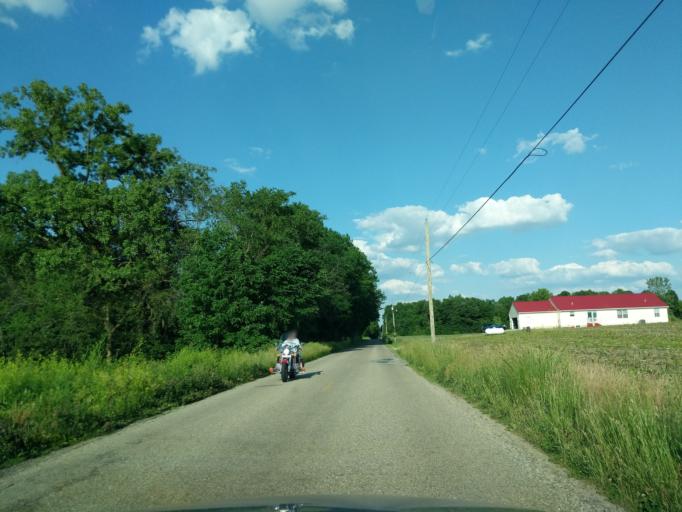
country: US
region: Indiana
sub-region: Kosciusko County
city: North Webster
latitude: 41.3026
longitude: -85.5762
